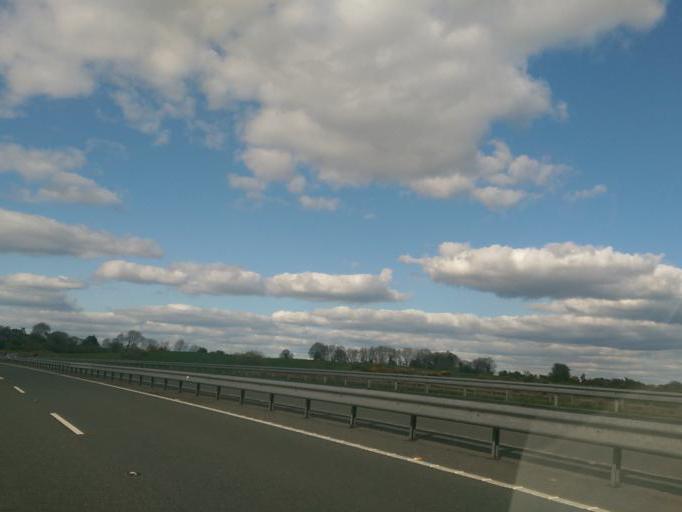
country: IE
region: Leinster
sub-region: An Iarmhi
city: Athlone
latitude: 53.3764
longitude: -8.0527
